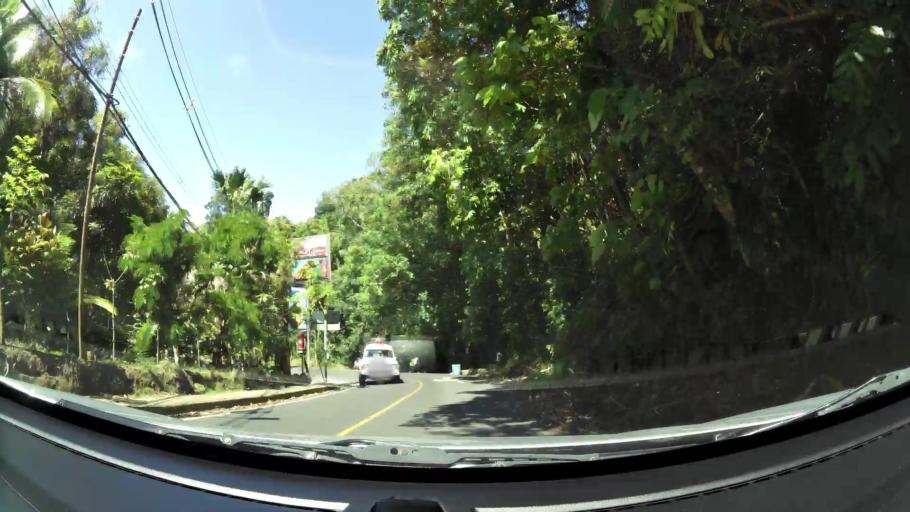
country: CR
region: Puntarenas
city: Quepos
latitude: 9.3927
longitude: -84.1505
